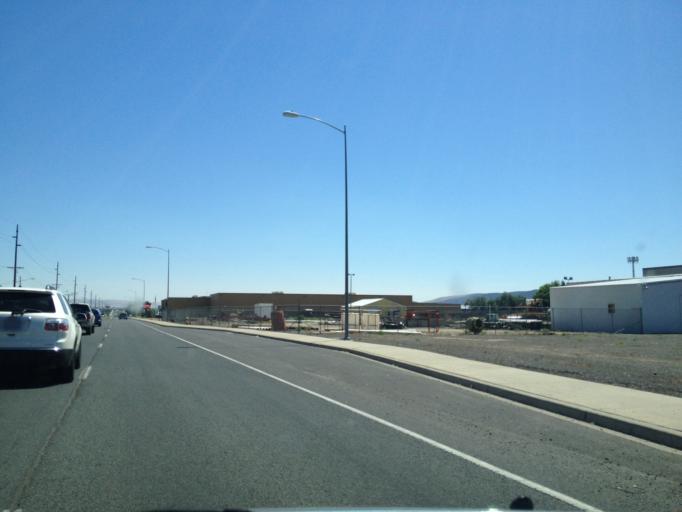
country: US
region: Washington
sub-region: Yakima County
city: Union Gap
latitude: 46.5634
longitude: -120.5094
